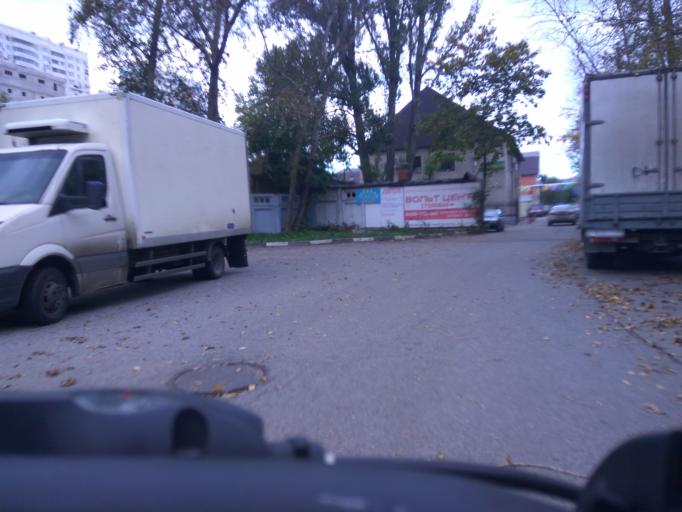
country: RU
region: Moscow
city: Otradnoye
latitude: 55.8739
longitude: 37.5949
